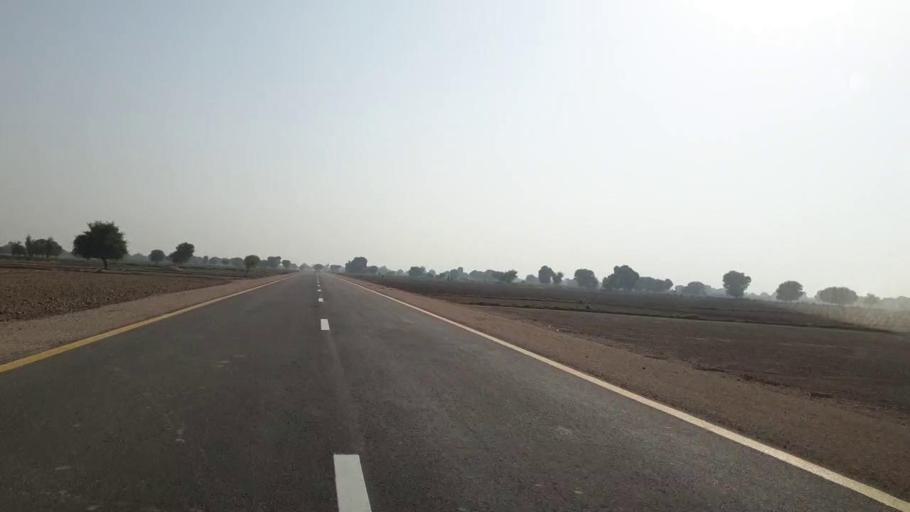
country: PK
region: Sindh
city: Bhan
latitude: 26.5149
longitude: 67.7861
